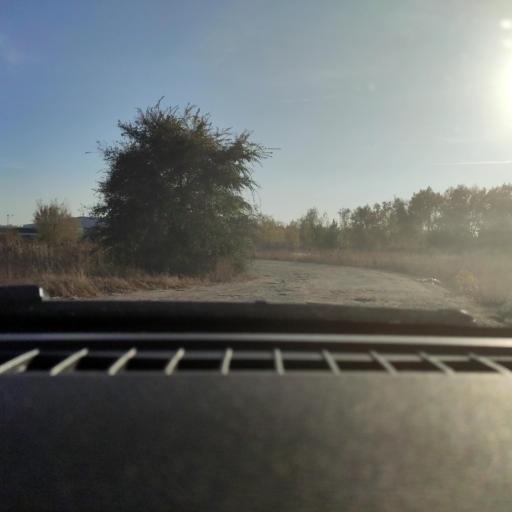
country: RU
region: Voronezj
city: Somovo
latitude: 51.6681
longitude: 39.2998
